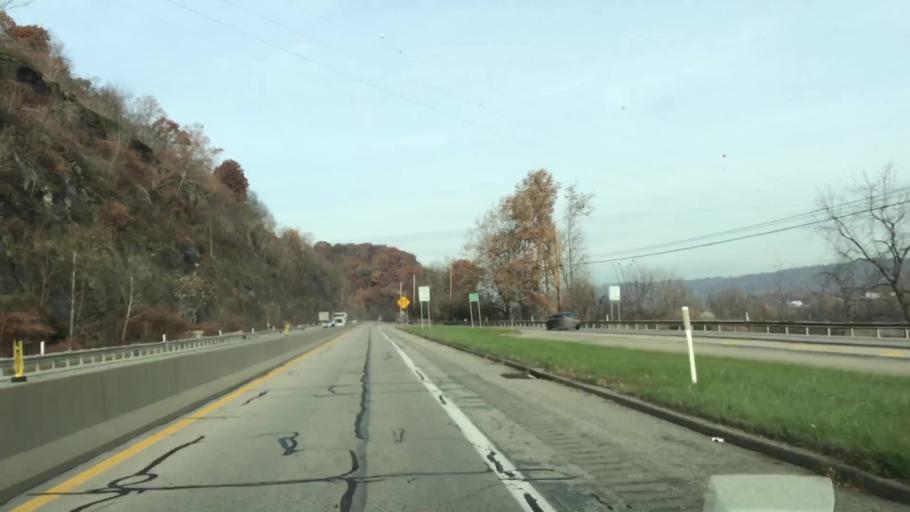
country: US
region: Pennsylvania
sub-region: Allegheny County
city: Sewickley
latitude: 40.5326
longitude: -80.1917
